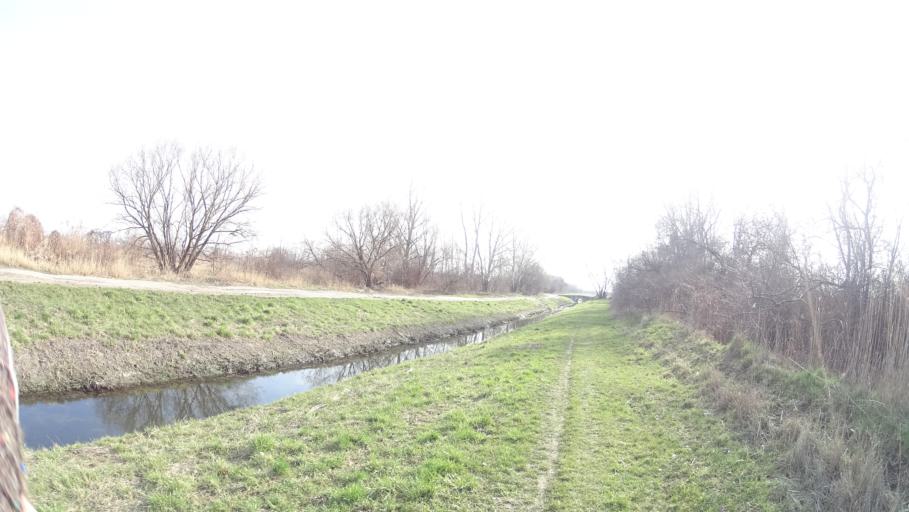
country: HU
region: Budapest
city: Budapest XIX. keruelet
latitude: 47.4154
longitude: 19.1484
